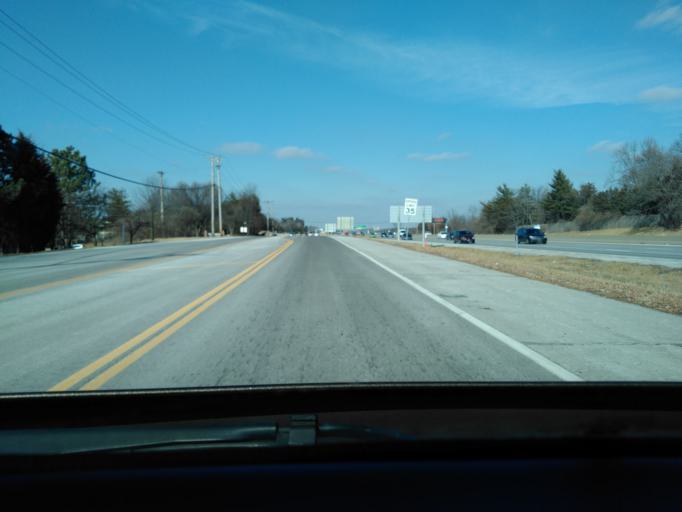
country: US
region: Missouri
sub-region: Saint Louis County
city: Manchester
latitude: 38.6308
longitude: -90.5145
